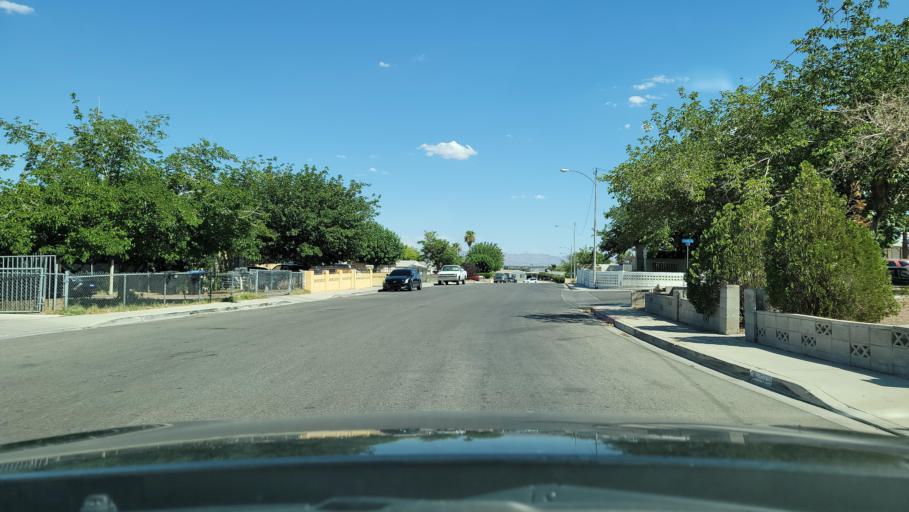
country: US
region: Nevada
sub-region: Clark County
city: Las Vegas
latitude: 36.2012
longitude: -115.1466
